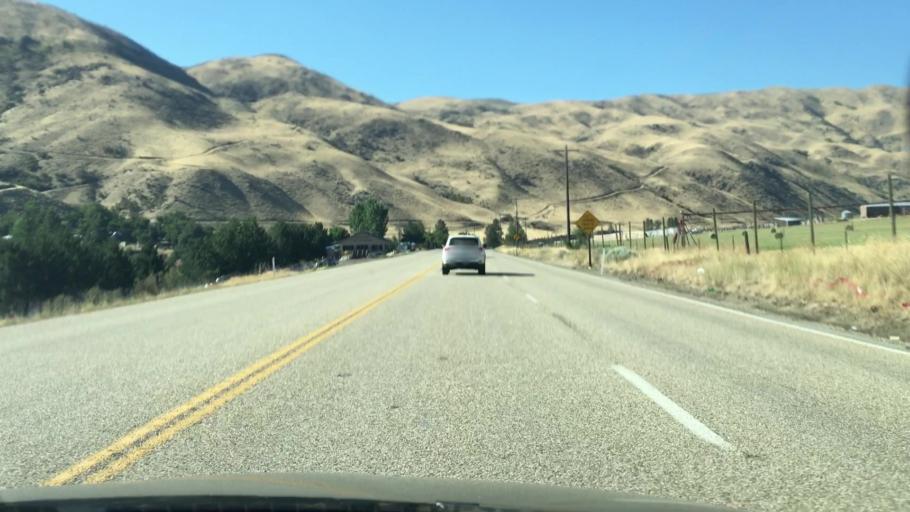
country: US
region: Idaho
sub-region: Gem County
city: Emmett
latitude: 43.9894
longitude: -116.1868
